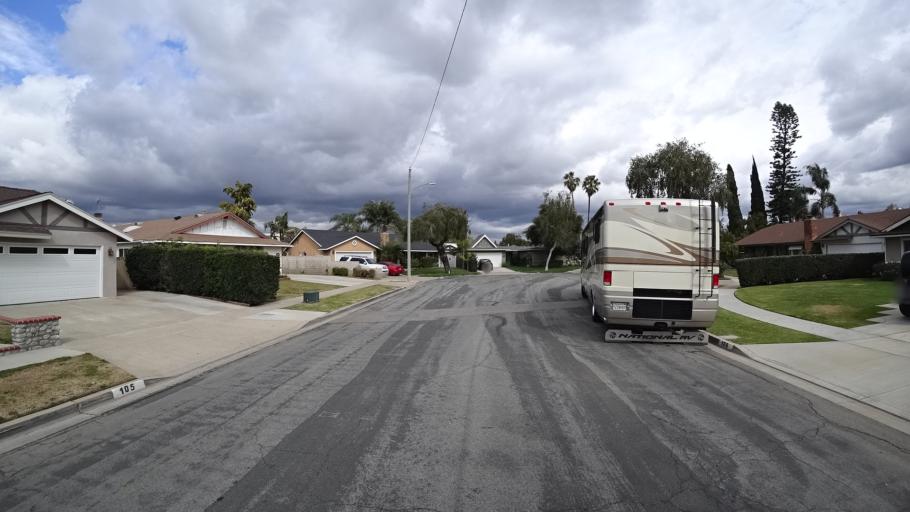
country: US
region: California
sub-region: Orange County
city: Placentia
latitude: 33.8415
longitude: -117.8656
